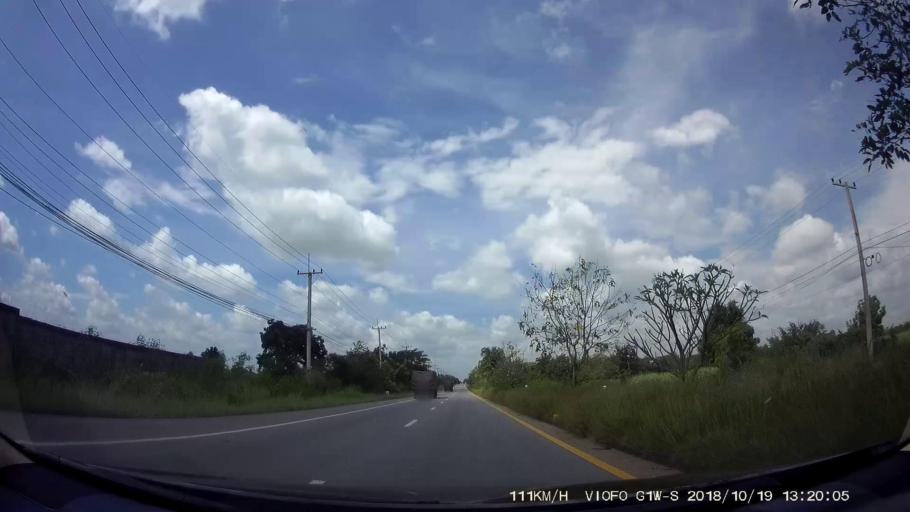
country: TH
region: Chaiyaphum
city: Chatturat
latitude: 15.4403
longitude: 101.8294
